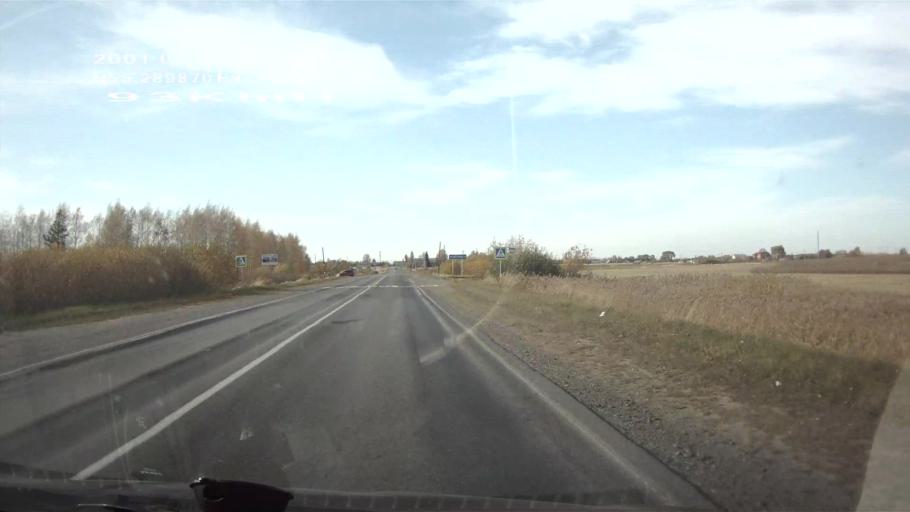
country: RU
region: Chuvashia
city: Ibresi
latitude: 55.2899
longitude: 47.0635
